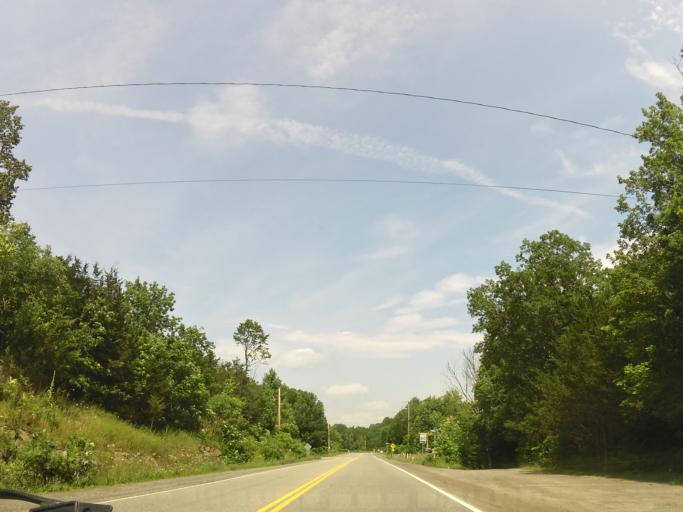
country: CA
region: Ontario
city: Kingston
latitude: 44.5487
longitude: -76.4384
